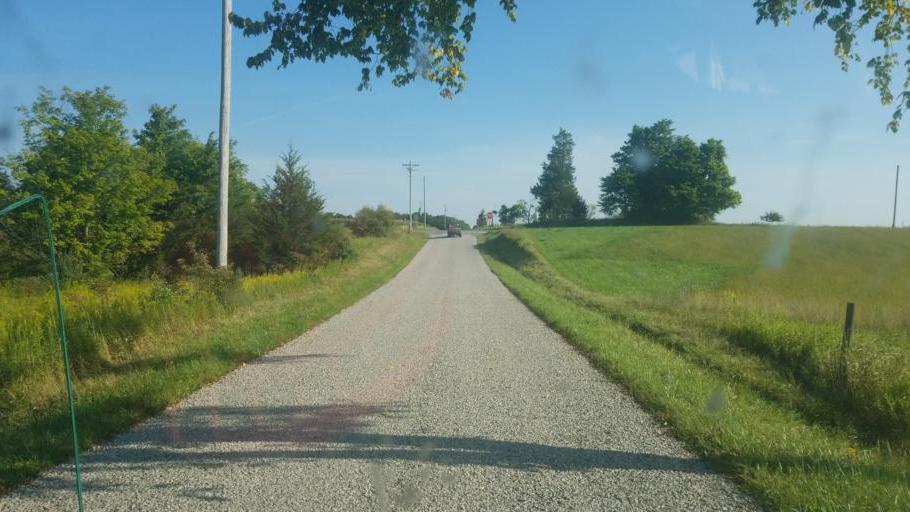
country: US
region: Ohio
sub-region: Ashland County
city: Ashland
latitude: 40.9571
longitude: -82.3400
